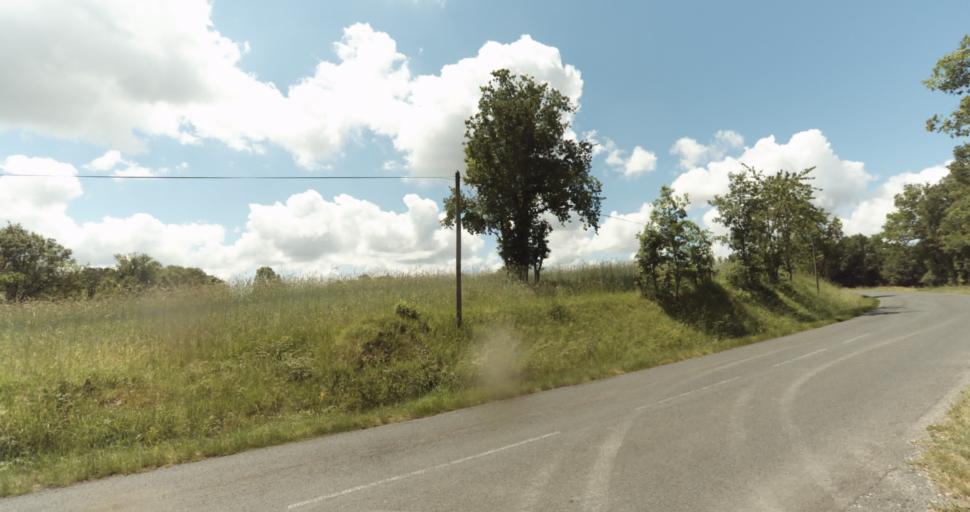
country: FR
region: Aquitaine
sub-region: Departement de la Dordogne
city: Beaumont-du-Perigord
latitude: 44.7512
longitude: 0.6907
